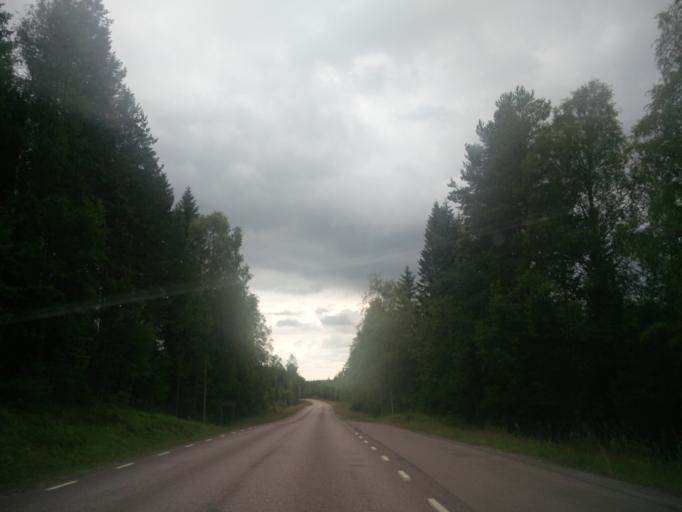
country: SE
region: Vaermland
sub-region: Arvika Kommun
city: Arvika
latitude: 59.9317
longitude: 12.6654
